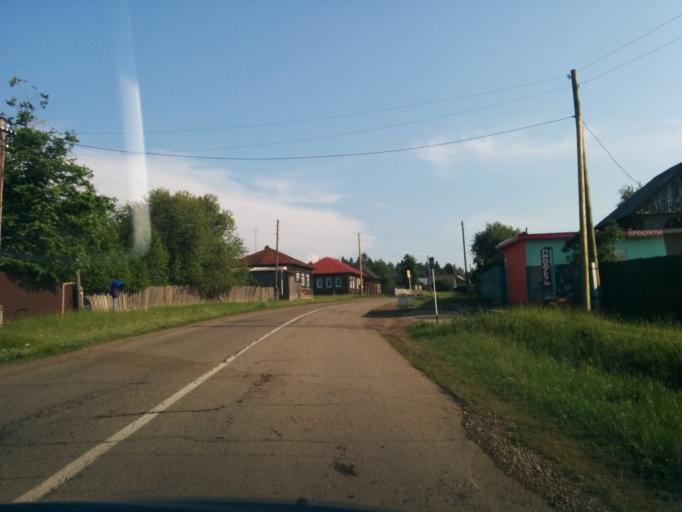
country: RU
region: Perm
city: Polazna
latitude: 58.2464
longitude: 56.2683
